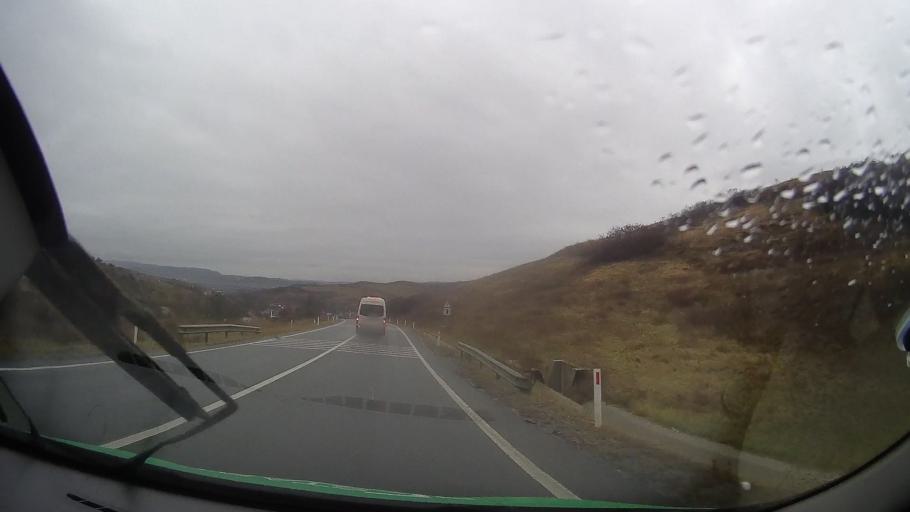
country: RO
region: Bistrita-Nasaud
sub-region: Comuna Galatii Bistritei
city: Galatii Bistritei
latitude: 47.0296
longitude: 24.4202
